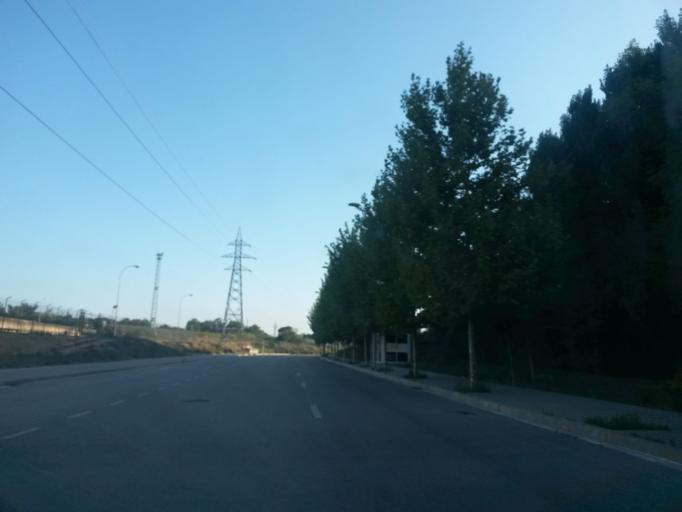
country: ES
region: Catalonia
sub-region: Provincia de Girona
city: Fornells de la Selva
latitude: 41.9487
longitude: 2.8014
